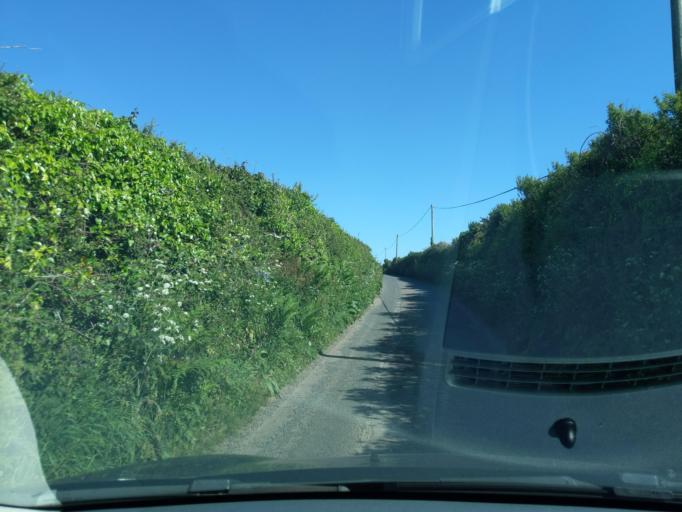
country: GB
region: England
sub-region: Cornwall
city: St. Buryan
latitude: 50.0646
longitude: -5.6012
